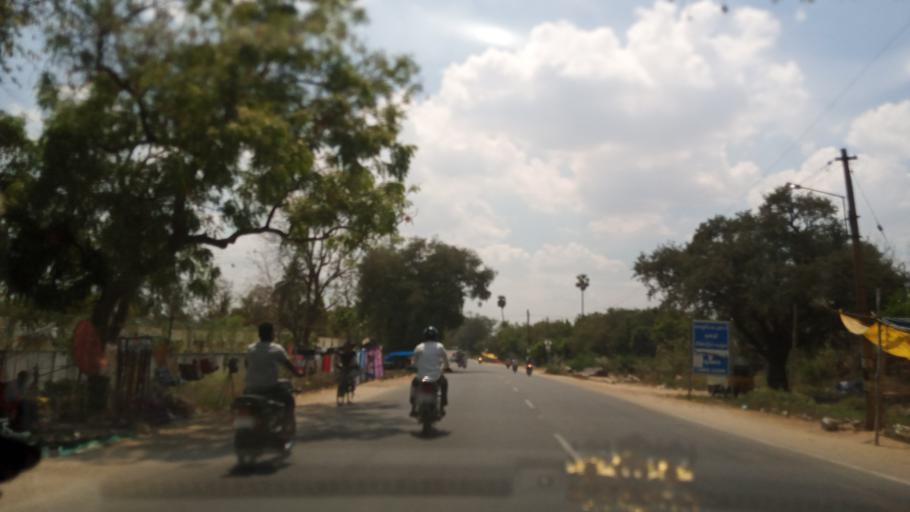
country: IN
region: Tamil Nadu
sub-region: Vellore
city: Walajapet
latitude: 12.9255
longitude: 79.3556
